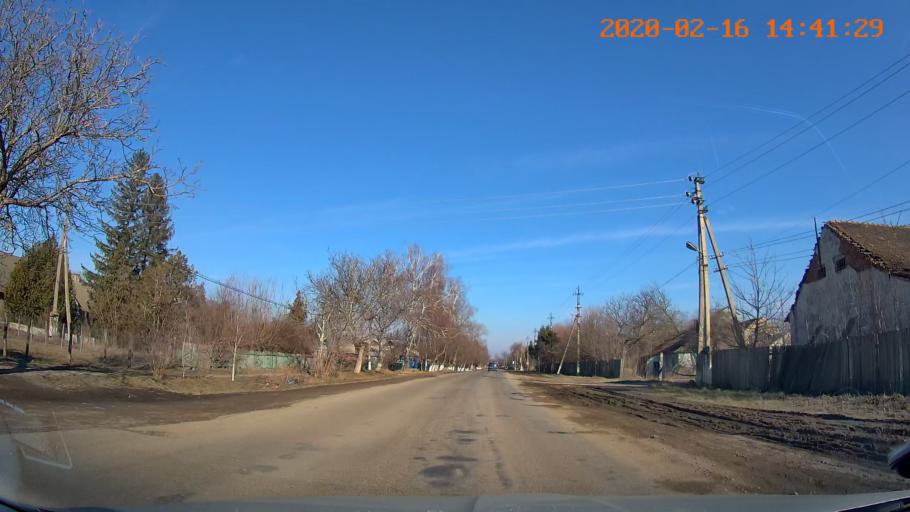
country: RO
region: Botosani
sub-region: Comuna Darabani
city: Bajura
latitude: 48.2536
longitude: 26.5727
